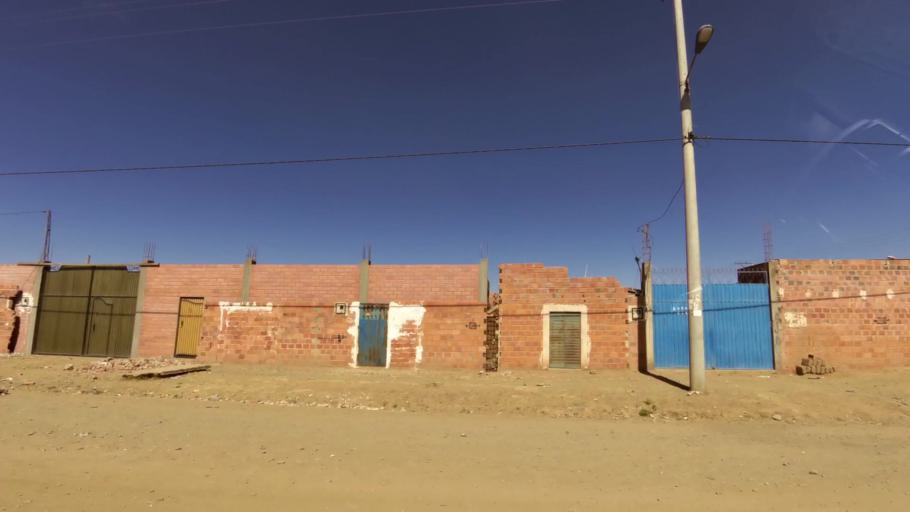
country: BO
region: La Paz
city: La Paz
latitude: -16.5869
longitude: -68.2054
